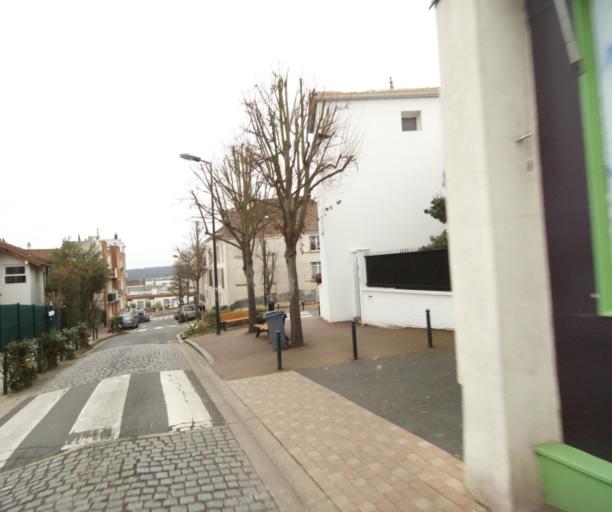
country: FR
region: Ile-de-France
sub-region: Departement des Hauts-de-Seine
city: Garches
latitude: 48.8466
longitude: 2.1893
